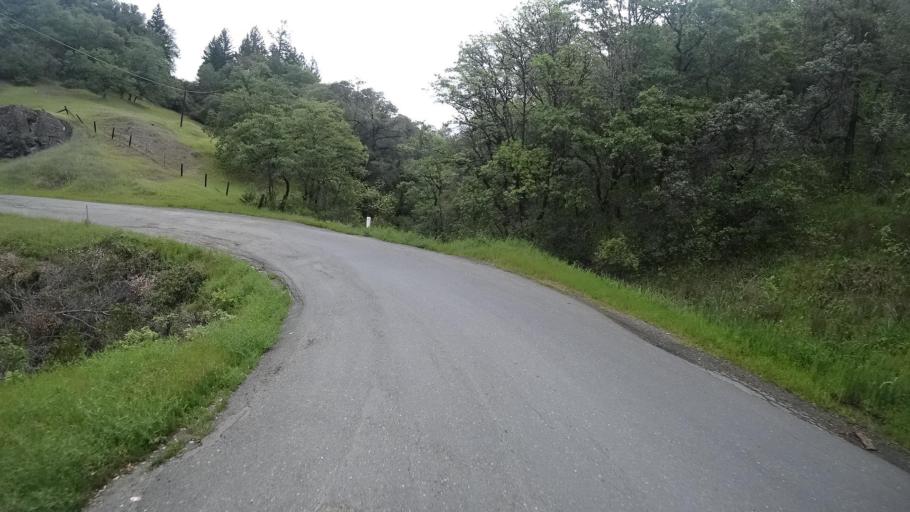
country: US
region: California
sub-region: Humboldt County
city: Redway
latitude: 40.1748
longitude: -123.5994
